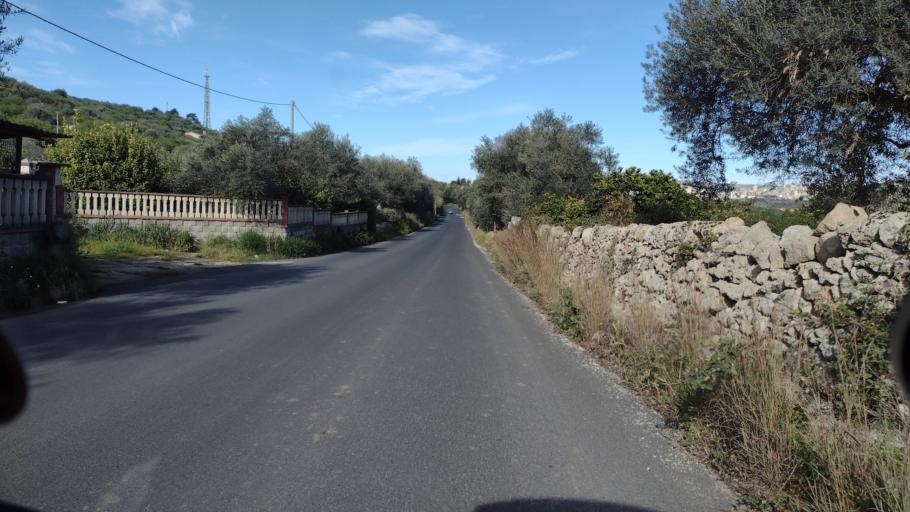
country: IT
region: Sicily
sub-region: Provincia di Siracusa
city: Noto
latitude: 36.8768
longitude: 15.0980
